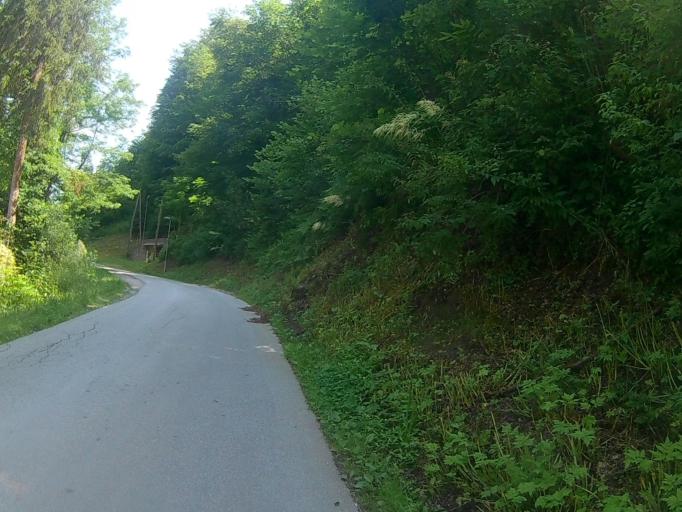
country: SI
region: Maribor
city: Bresternica
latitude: 46.5715
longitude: 15.5766
